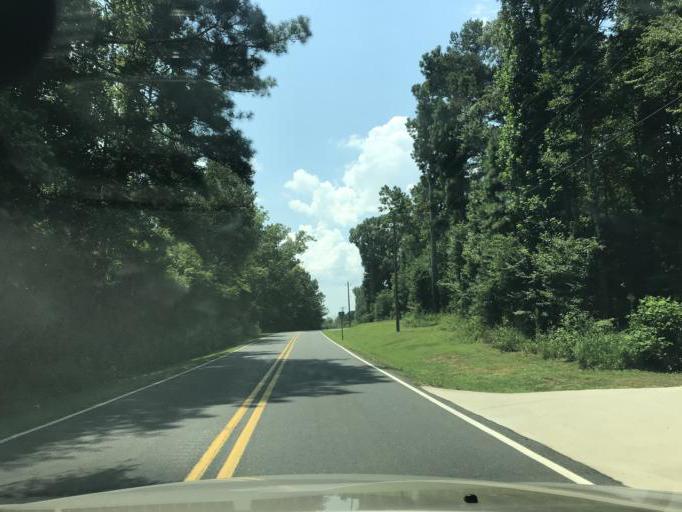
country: US
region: Georgia
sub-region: Dawson County
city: Dawsonville
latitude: 34.3254
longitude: -84.1609
